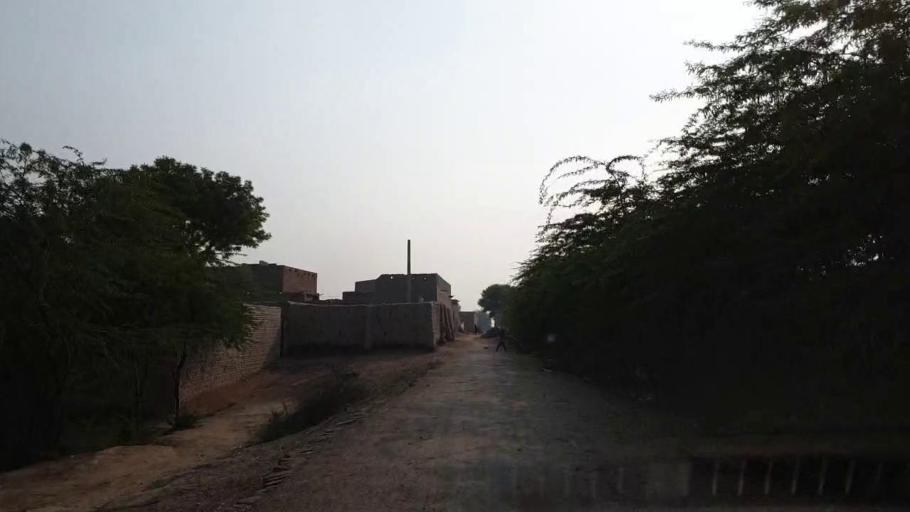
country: PK
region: Sindh
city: Bhan
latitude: 26.5607
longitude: 67.7037
